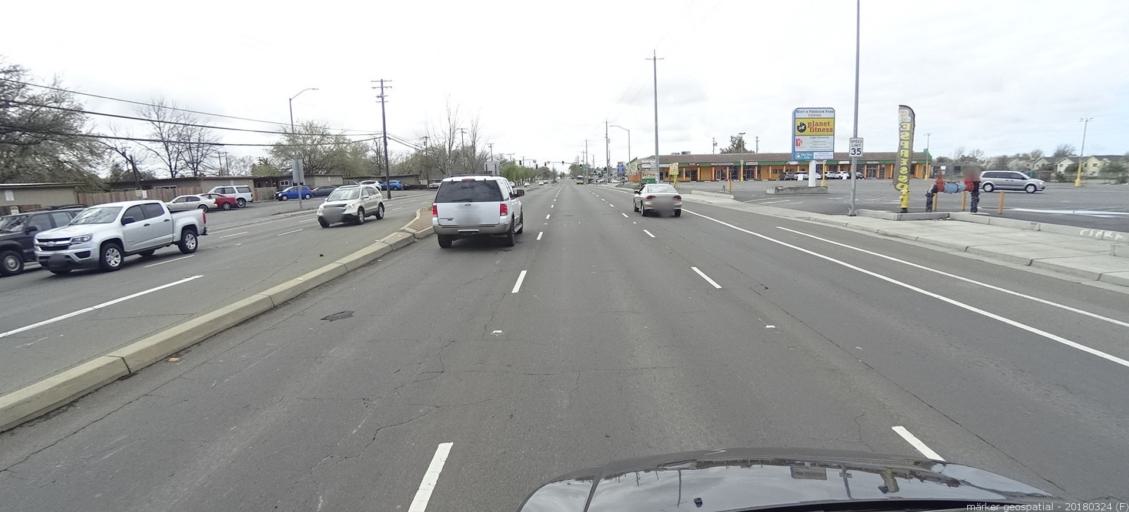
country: US
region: California
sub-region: Sacramento County
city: North Highlands
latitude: 38.6754
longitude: -121.3830
